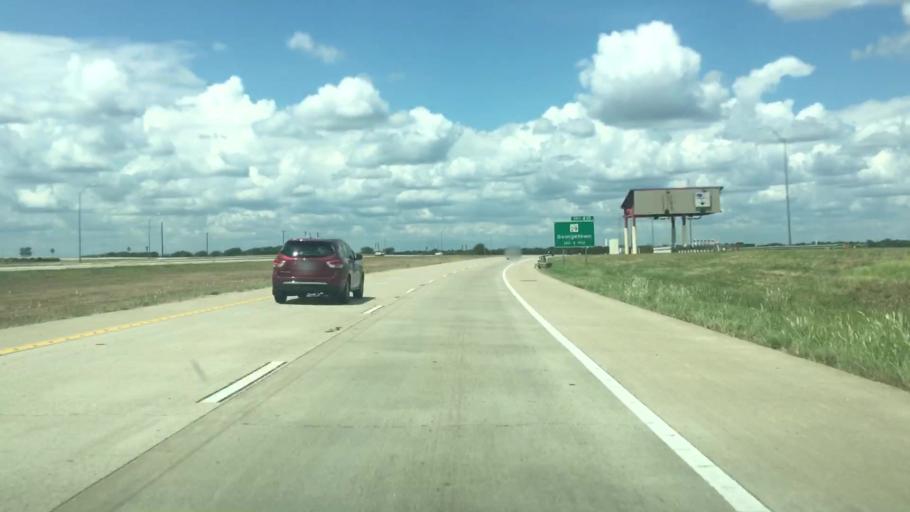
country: US
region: Texas
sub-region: Williamson County
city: Georgetown
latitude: 30.6238
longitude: -97.6207
